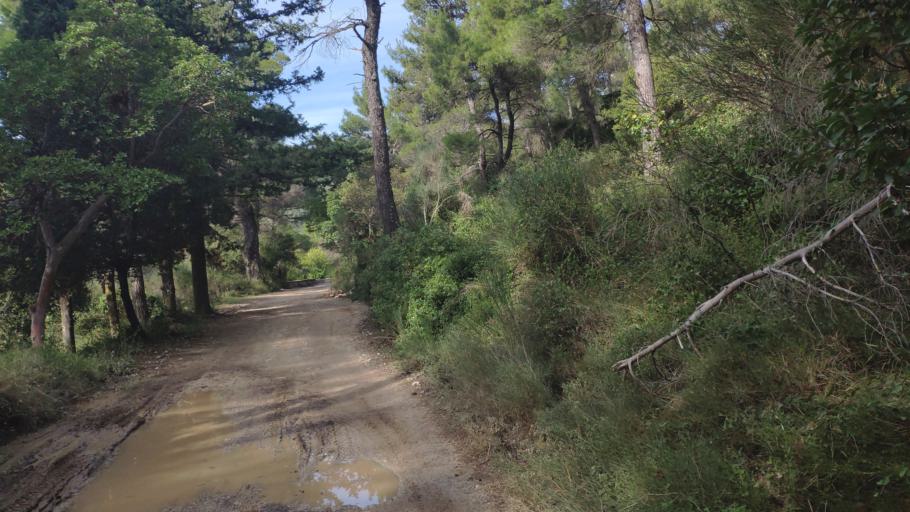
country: GR
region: Attica
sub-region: Nomarchia Anatolikis Attikis
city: Varybobi
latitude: 38.1637
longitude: 23.7879
